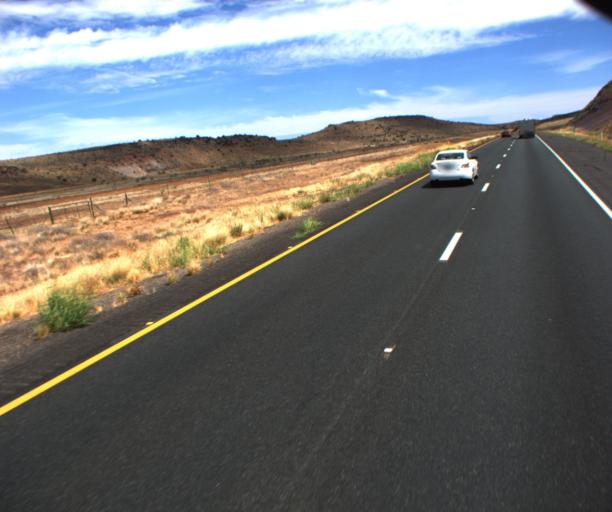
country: US
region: Arizona
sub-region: Yavapai County
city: Cordes Lakes
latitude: 34.4442
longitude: -112.0309
